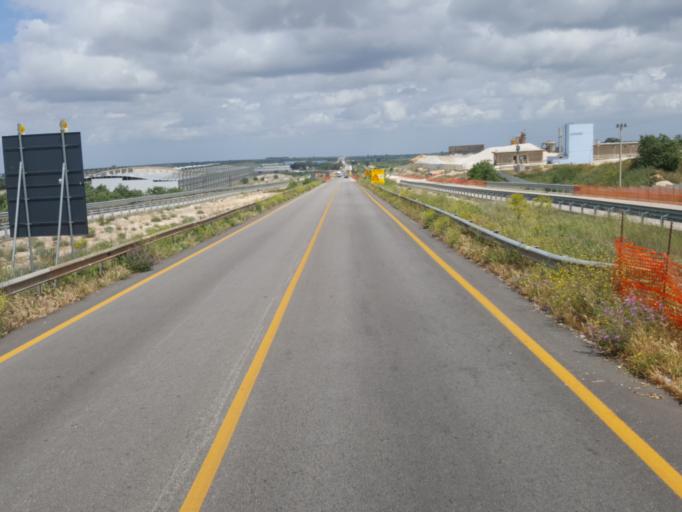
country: IT
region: Apulia
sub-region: Provincia di Bari
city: Quasano
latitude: 40.9253
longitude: 16.6329
